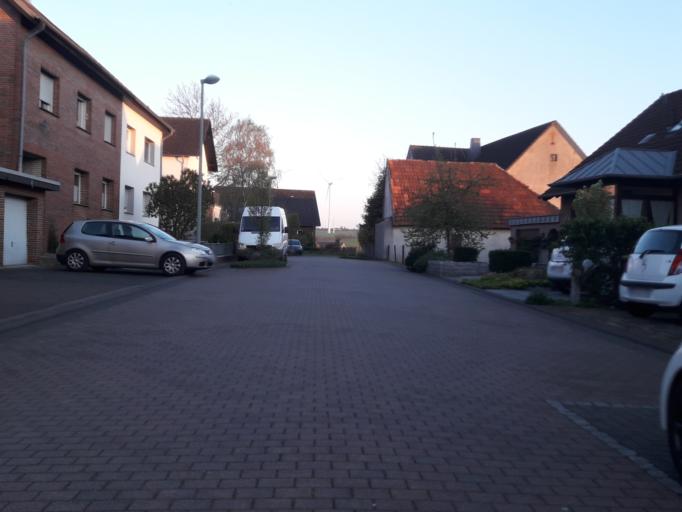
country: DE
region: North Rhine-Westphalia
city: Bad Lippspringe
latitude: 51.7385
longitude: 8.8171
